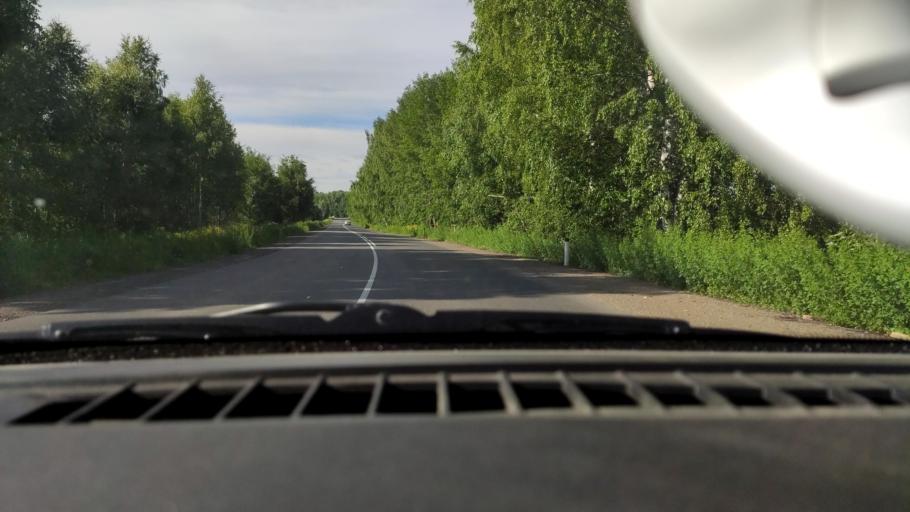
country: RU
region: Perm
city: Nytva
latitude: 57.9292
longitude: 55.4499
